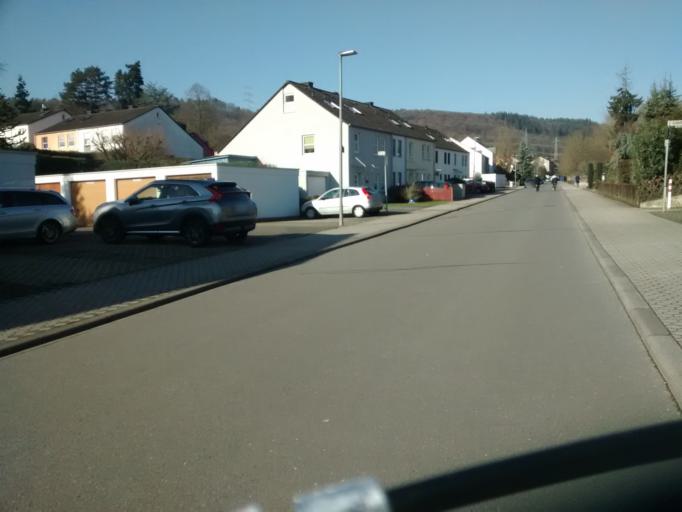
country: DE
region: Rheinland-Pfalz
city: Kenn
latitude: 49.8222
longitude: 6.7084
